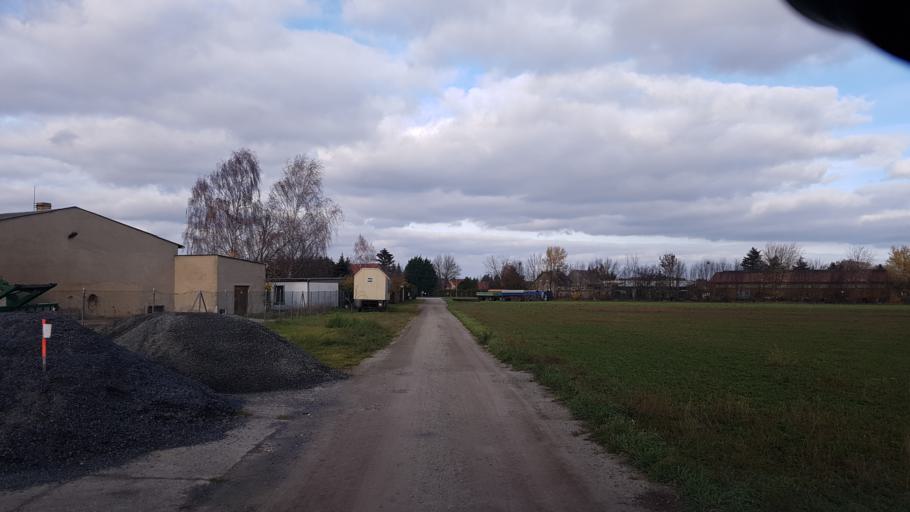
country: DE
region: Brandenburg
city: Sallgast
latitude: 51.6037
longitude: 13.8640
